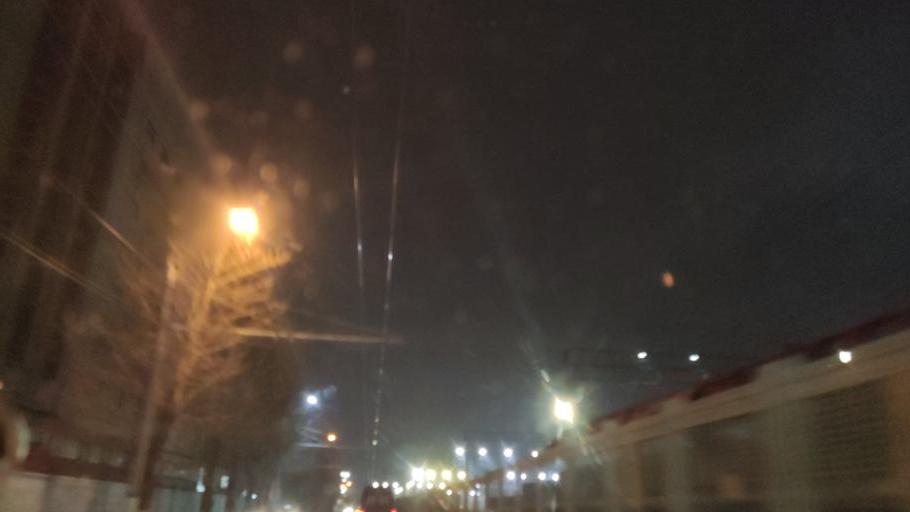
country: RU
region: Moskovskaya
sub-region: Podol'skiy Rayon
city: Podol'sk
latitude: 55.4285
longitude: 37.5646
